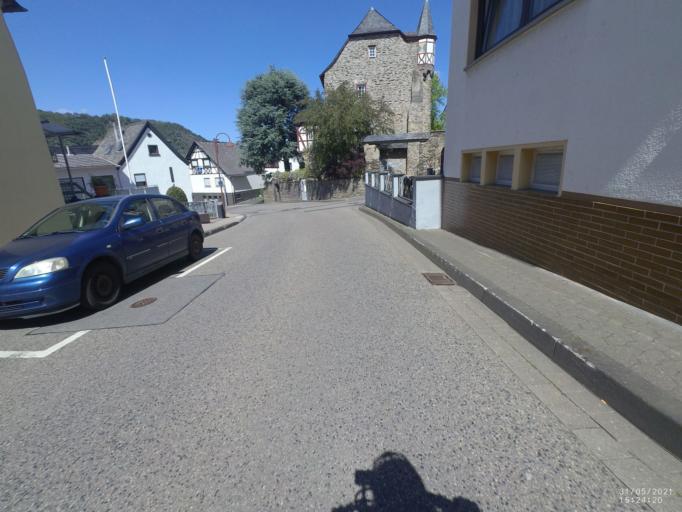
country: DE
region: Rheinland-Pfalz
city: Dieblich
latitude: 50.3130
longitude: 7.4678
